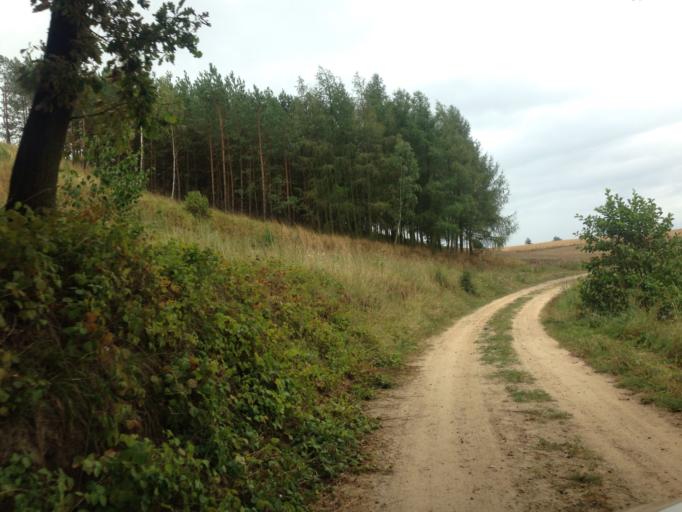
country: PL
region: Kujawsko-Pomorskie
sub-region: Powiat brodnicki
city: Bartniczka
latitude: 53.2735
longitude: 19.6382
